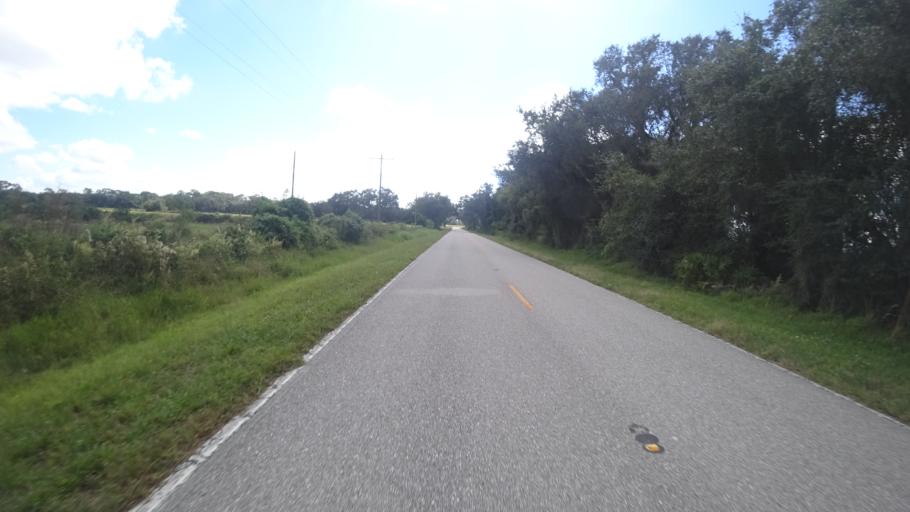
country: US
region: Florida
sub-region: Sarasota County
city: Lake Sarasota
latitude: 27.3275
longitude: -82.1667
